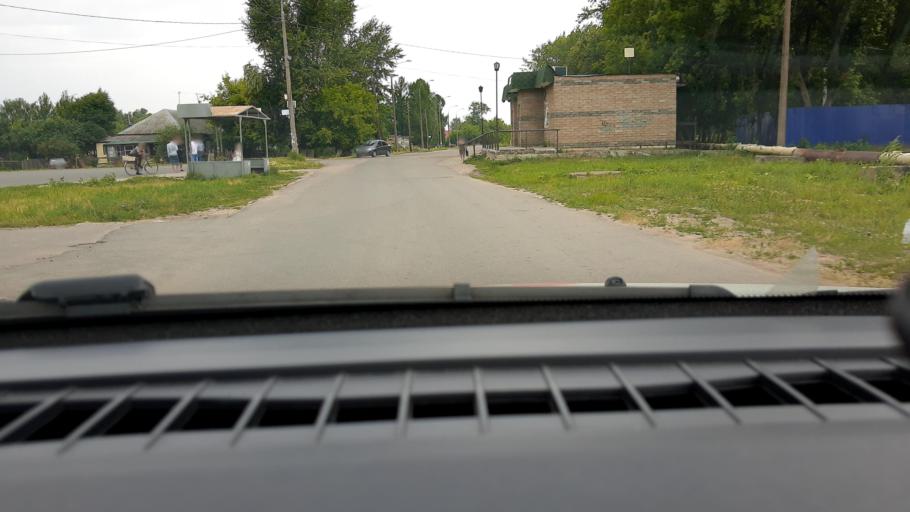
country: RU
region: Nizjnij Novgorod
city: Gorbatovka
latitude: 56.2457
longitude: 43.7487
